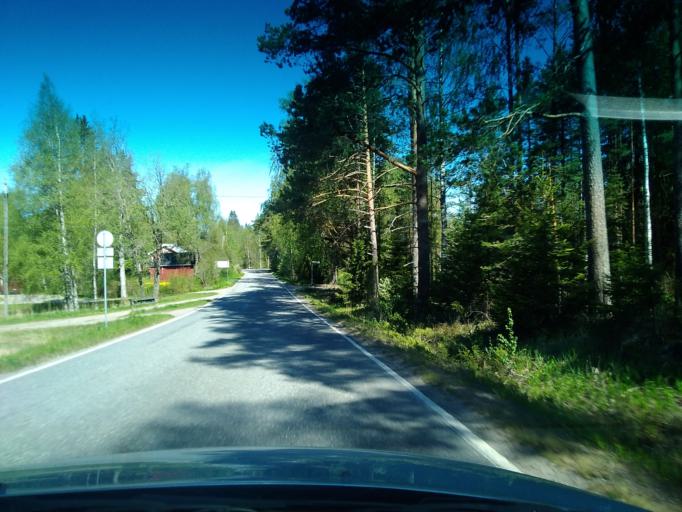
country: FI
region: Uusimaa
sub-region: Helsinki
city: Kaerkoelae
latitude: 60.7060
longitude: 23.9295
